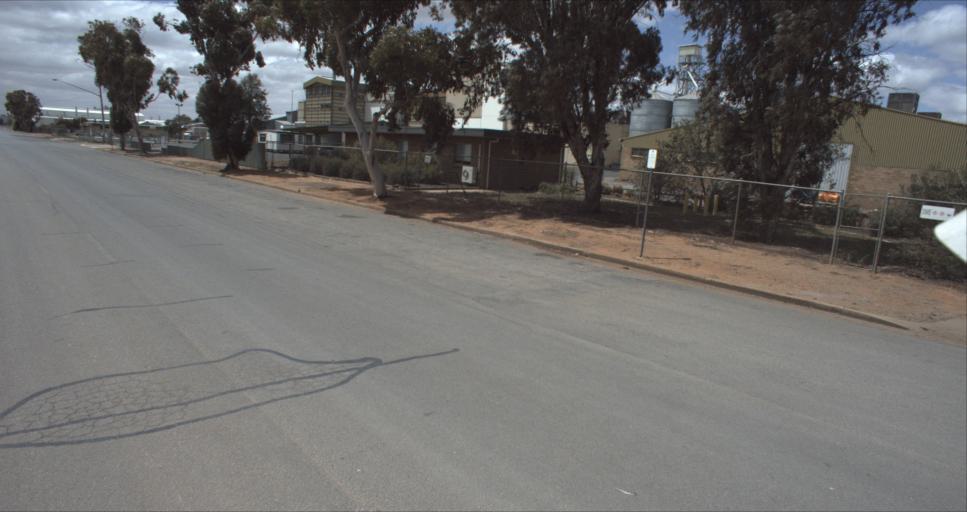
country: AU
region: New South Wales
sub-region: Leeton
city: Leeton
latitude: -34.5573
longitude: 146.3920
